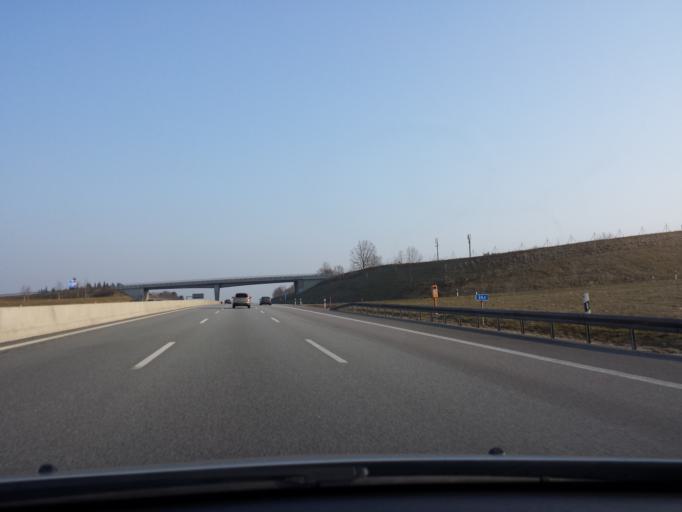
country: DE
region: Bavaria
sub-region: Upper Bavaria
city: Odelzhausen
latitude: 48.3092
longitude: 11.2052
